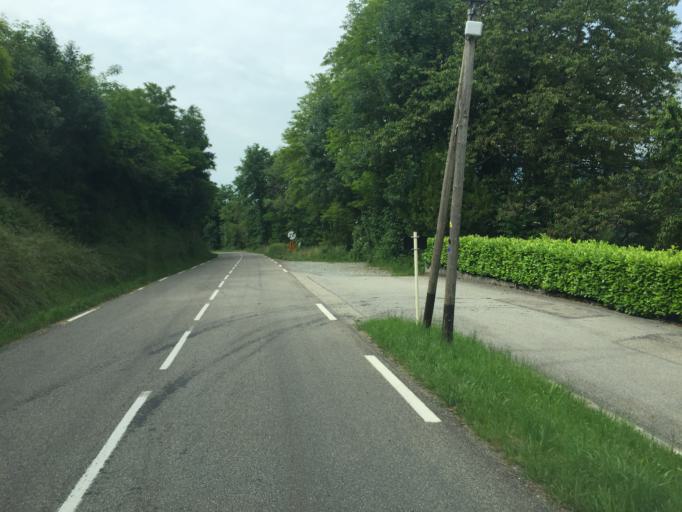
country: FR
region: Rhone-Alpes
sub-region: Departement de la Savoie
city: Jacob-Bellecombette
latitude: 45.5243
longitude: 5.9159
